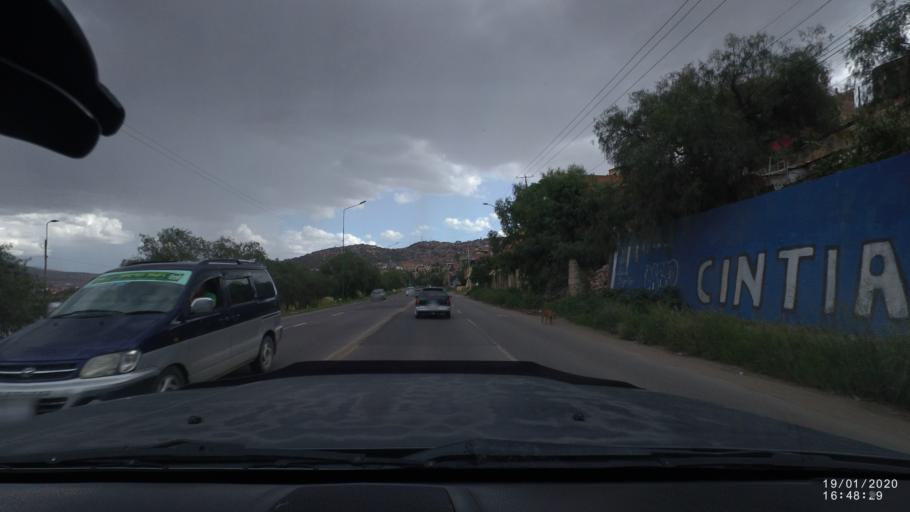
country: BO
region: Cochabamba
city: Cochabamba
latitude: -17.4109
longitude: -66.1425
